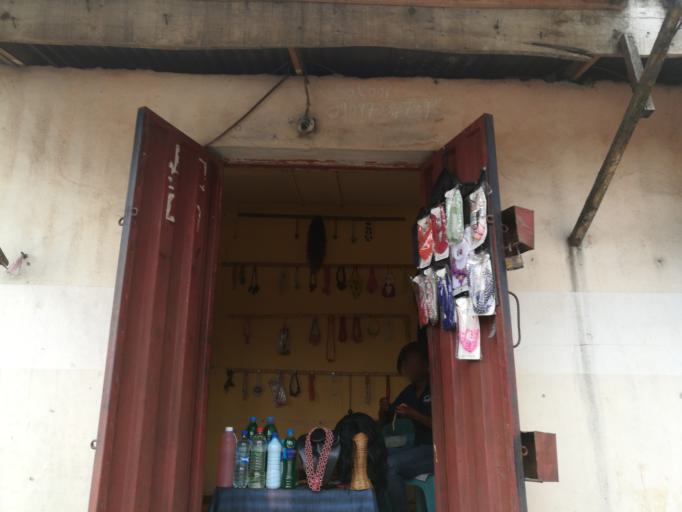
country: NG
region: Rivers
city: Okrika
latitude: 4.7322
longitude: 7.1529
